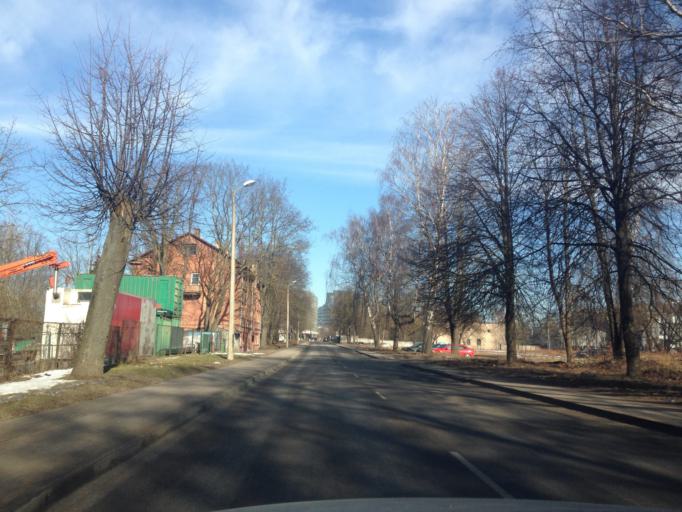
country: LV
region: Riga
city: Riga
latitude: 56.9332
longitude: 24.0989
